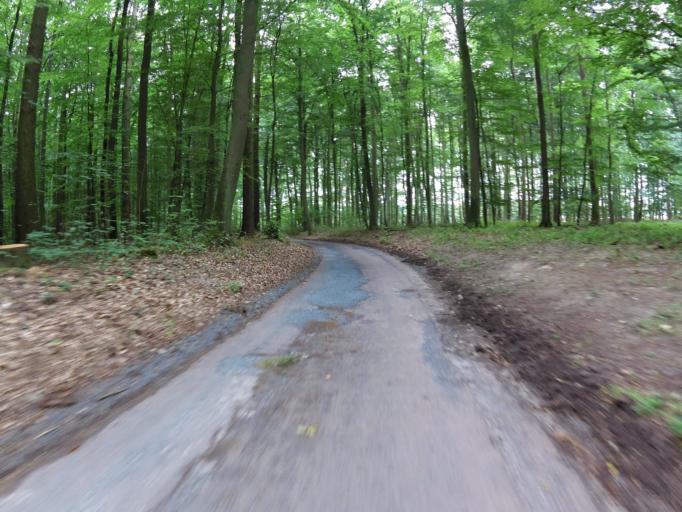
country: DE
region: Mecklenburg-Vorpommern
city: Seebad Heringsdorf
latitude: 53.8975
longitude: 14.1636
